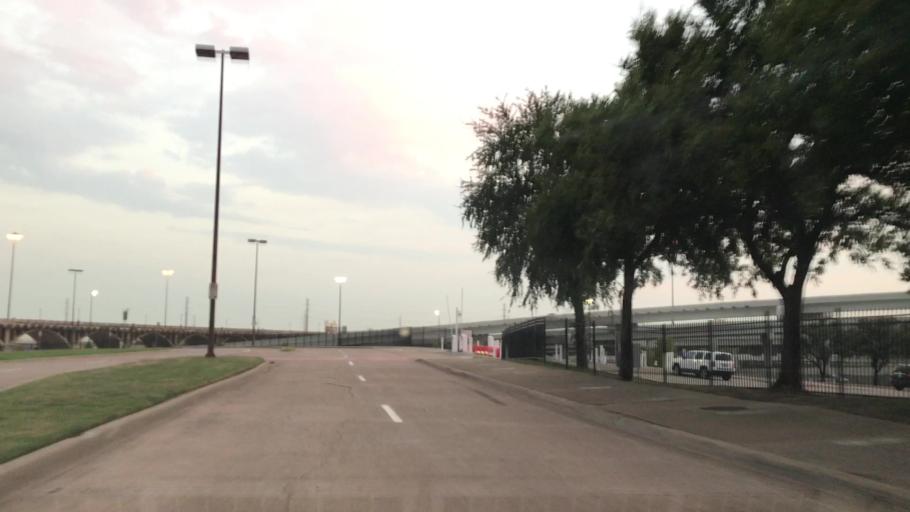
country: US
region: Texas
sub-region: Dallas County
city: Dallas
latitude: 32.7734
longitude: -96.8090
